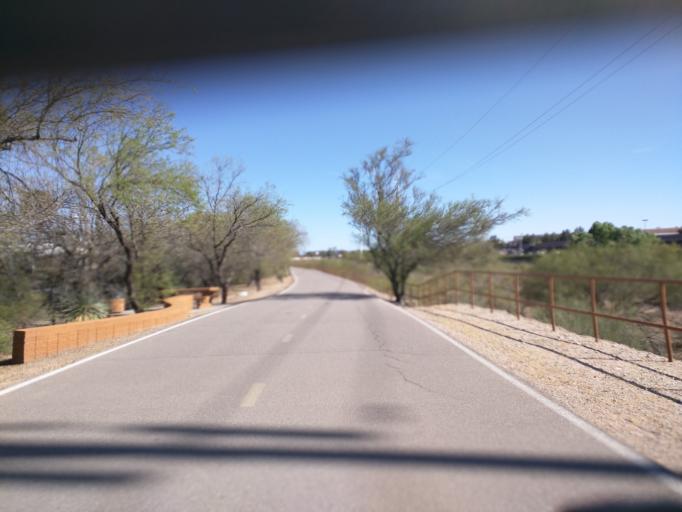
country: US
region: Arizona
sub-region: Pima County
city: Flowing Wells
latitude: 32.2930
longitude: -110.9746
